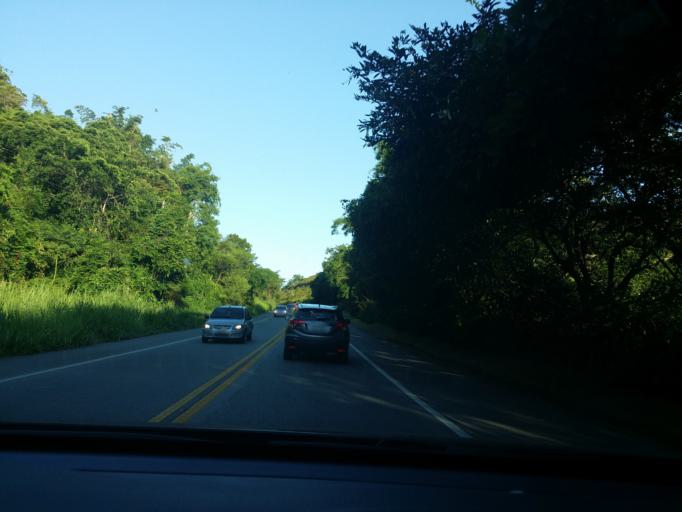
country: BR
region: Sao Paulo
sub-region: Sao Sebastiao
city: Sao Sebastiao
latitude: -23.7707
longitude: -45.7062
